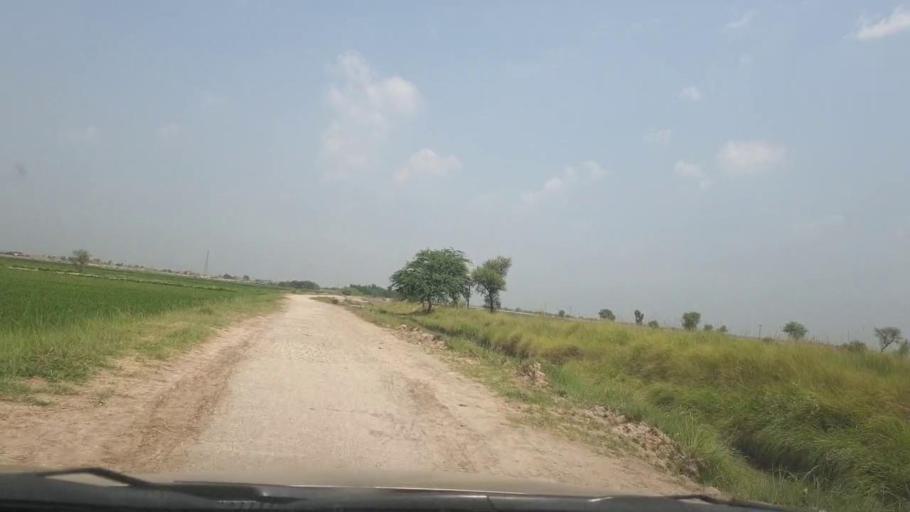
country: PK
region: Sindh
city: Ratodero
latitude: 27.6910
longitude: 68.2333
